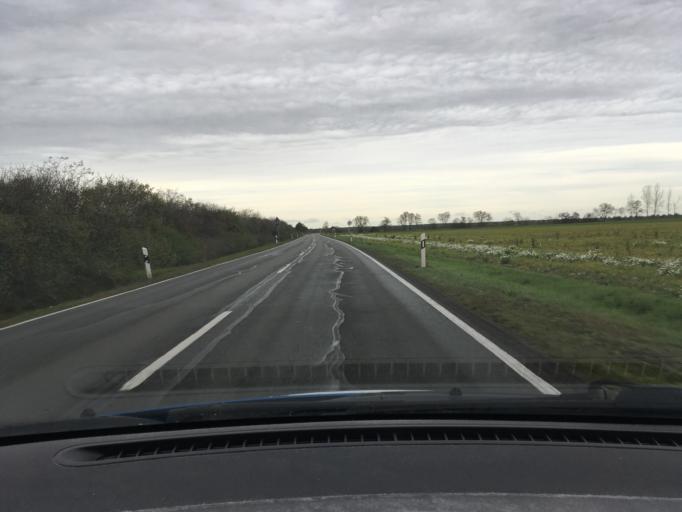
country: DE
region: Saxony-Anhalt
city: Zerbst
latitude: 52.0050
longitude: 12.0272
